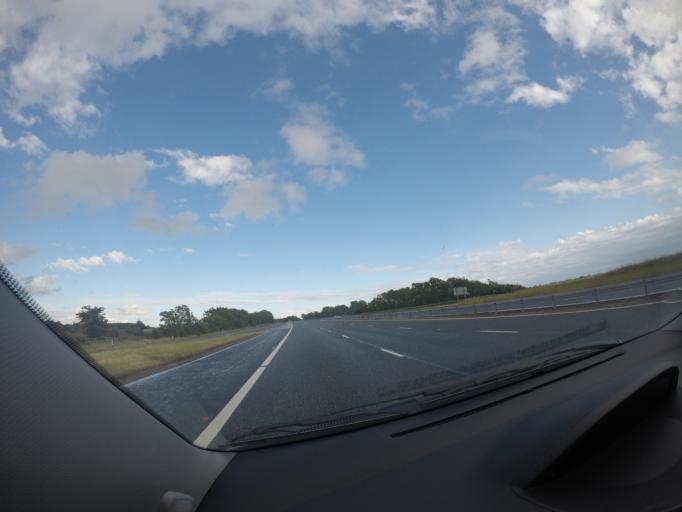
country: GB
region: Scotland
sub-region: Dumfries and Galloway
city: Annan
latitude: 55.0511
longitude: -3.2167
